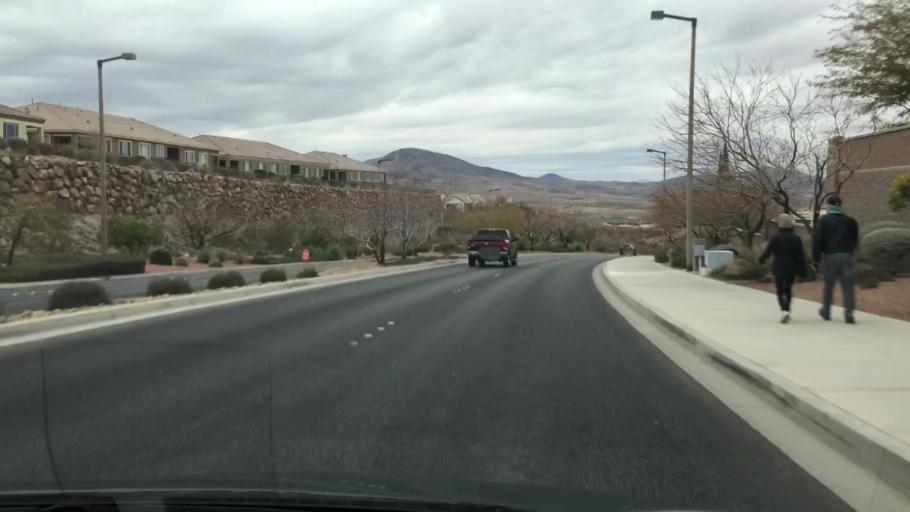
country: US
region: Nevada
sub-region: Clark County
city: Whitney
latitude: 35.9418
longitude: -115.1029
